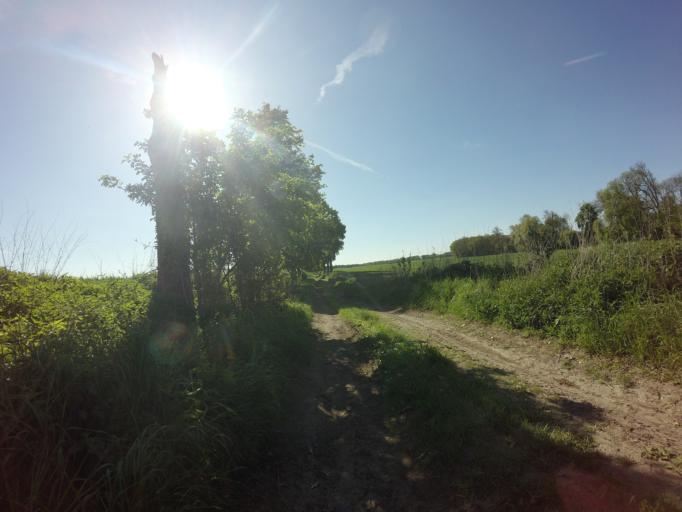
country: PL
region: West Pomeranian Voivodeship
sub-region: Powiat stargardzki
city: Dolice
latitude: 53.1571
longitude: 15.3083
